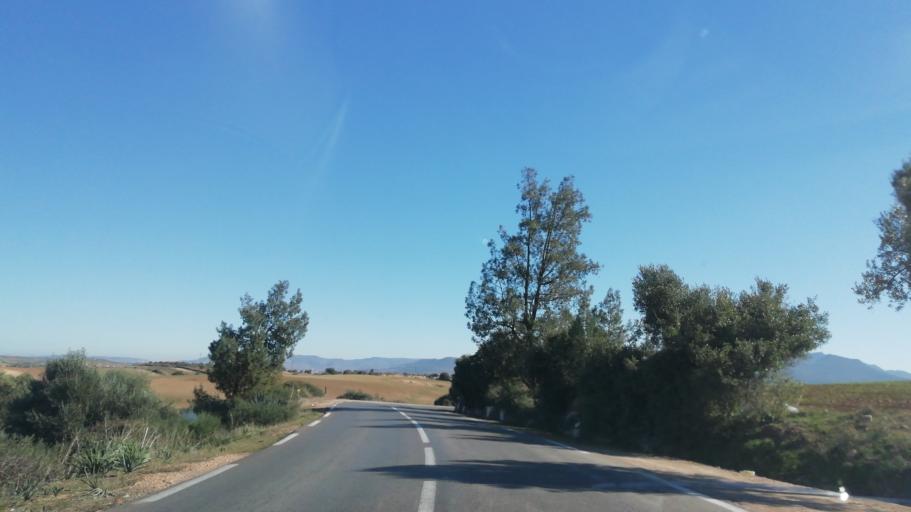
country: DZ
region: Tlemcen
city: Beni Mester
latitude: 34.8282
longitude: -1.5881
